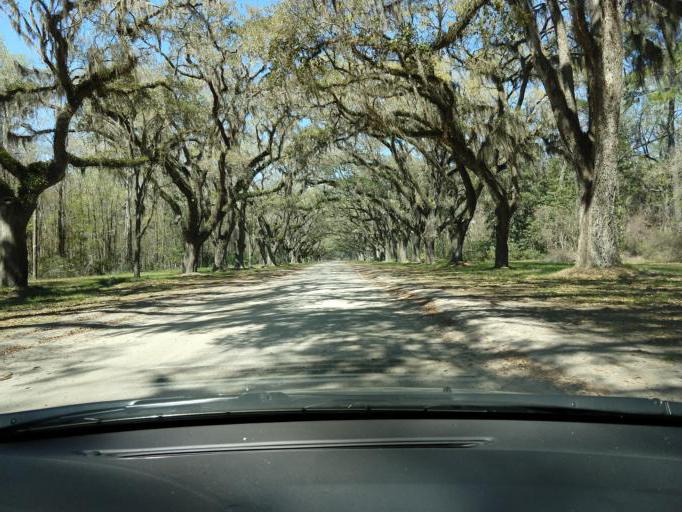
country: US
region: Georgia
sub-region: Chatham County
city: Isle of Hope
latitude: 31.9733
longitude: -81.0691
